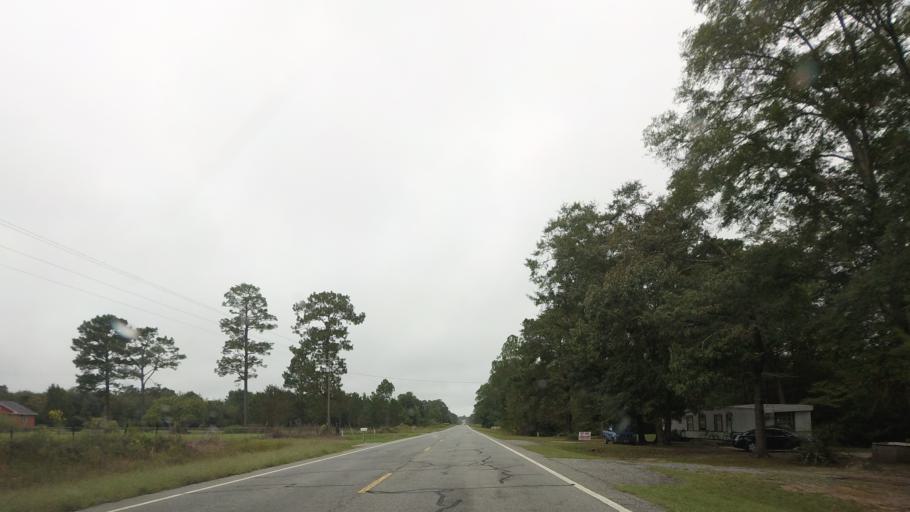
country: US
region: Georgia
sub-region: Irwin County
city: Ocilla
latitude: 31.4904
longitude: -83.2384
